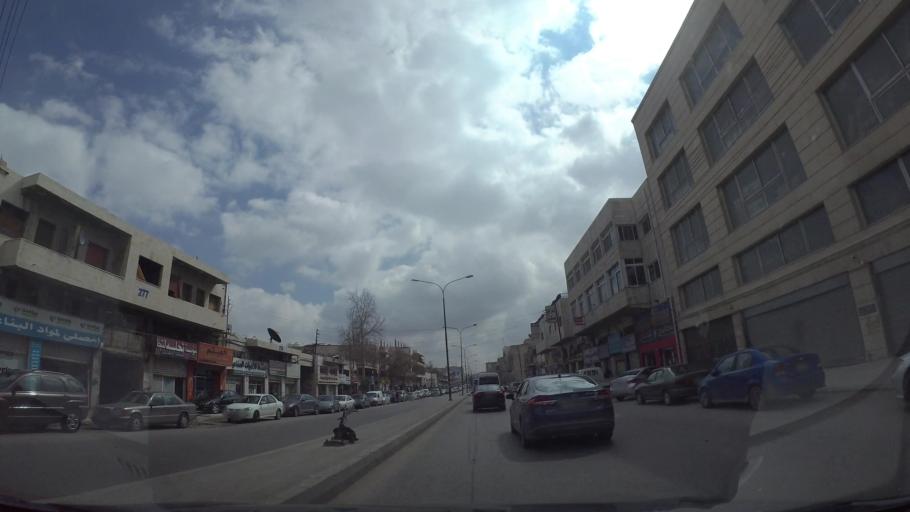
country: JO
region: Amman
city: Al Quwaysimah
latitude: 31.9250
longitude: 35.9379
